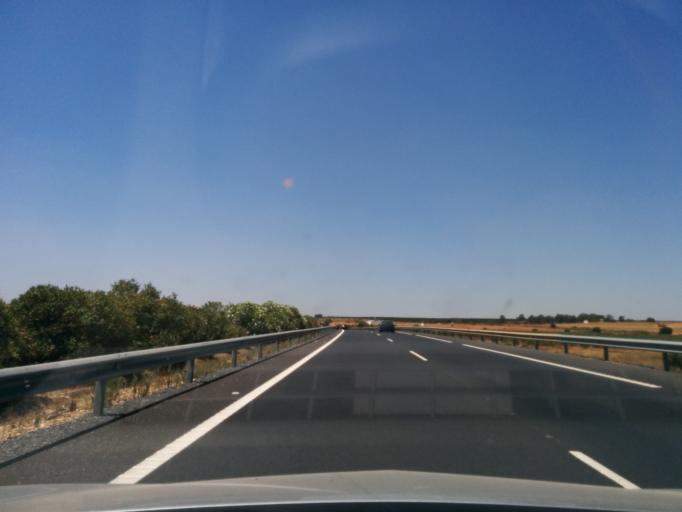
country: ES
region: Andalusia
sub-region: Provincia de Huelva
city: Lucena del Puerto
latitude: 37.3410
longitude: -6.7213
